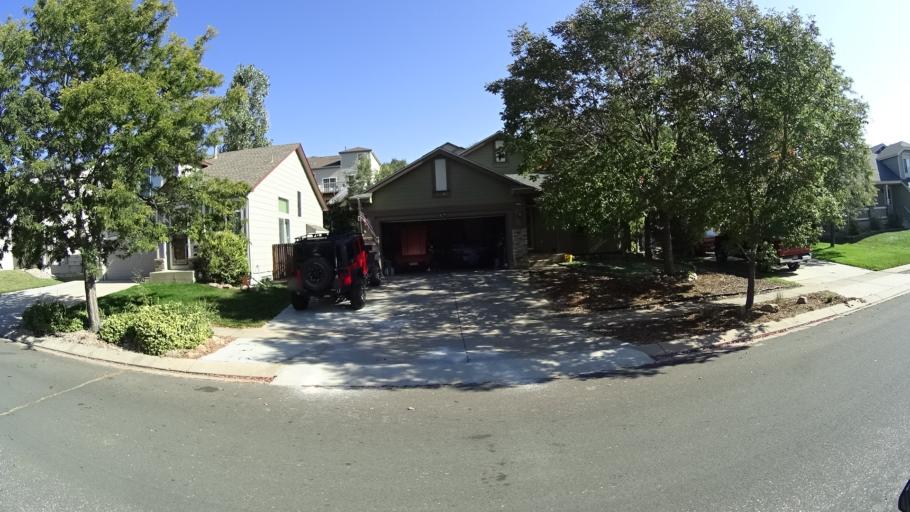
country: US
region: Colorado
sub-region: El Paso County
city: Cimarron Hills
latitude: 38.8807
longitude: -104.7039
